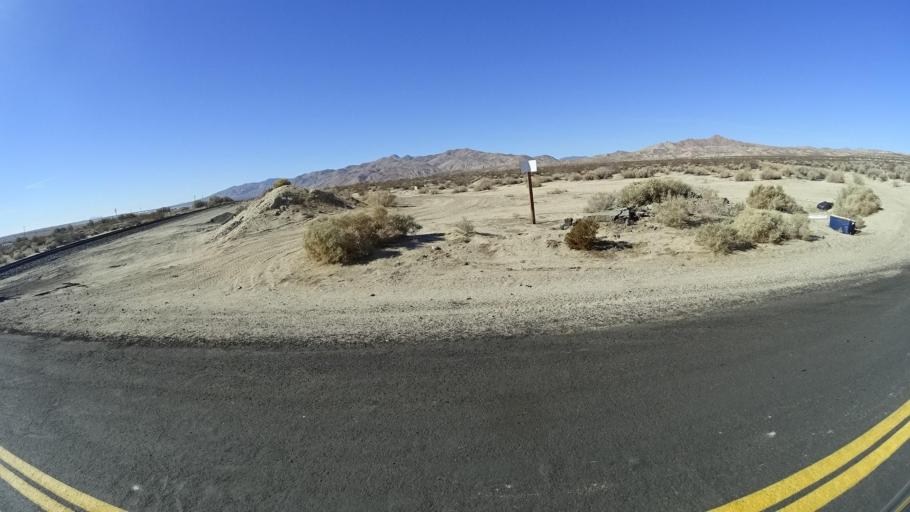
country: US
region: California
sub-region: Kern County
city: California City
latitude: 35.3116
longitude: -117.9650
